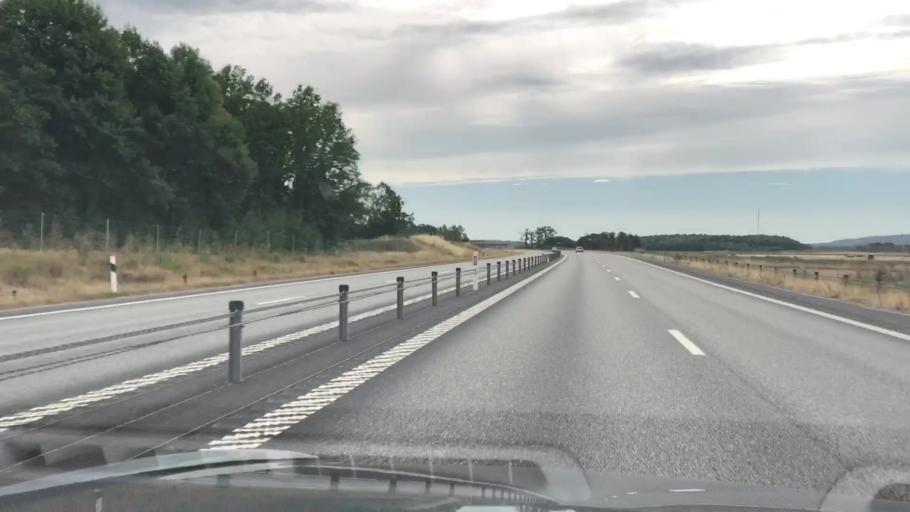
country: SE
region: Blekinge
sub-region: Karlshamns Kommun
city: Morrum
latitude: 56.1393
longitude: 14.6612
